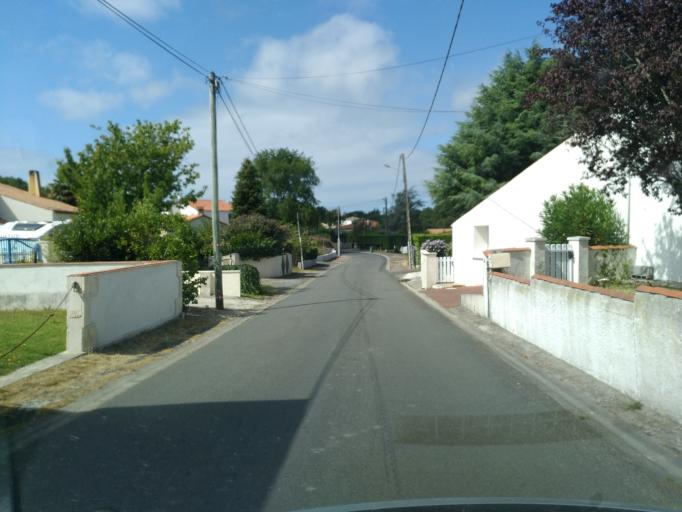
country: FR
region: Poitou-Charentes
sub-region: Departement de la Charente-Maritime
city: Breuillet
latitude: 45.6890
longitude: -1.0721
